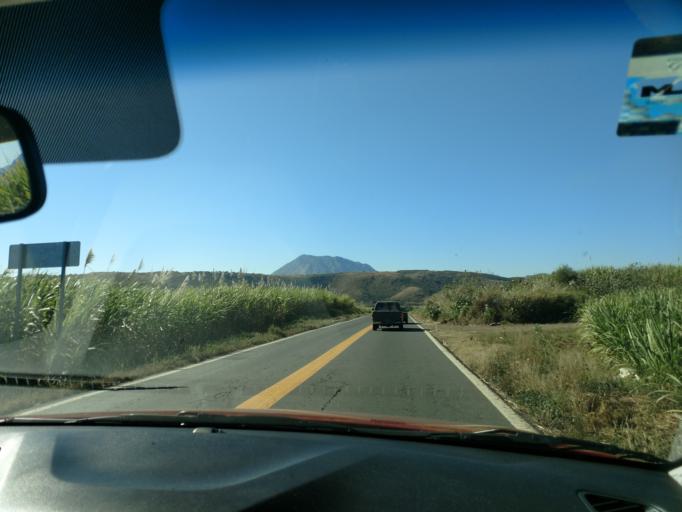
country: MX
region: Nayarit
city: San Pedro Lagunillas
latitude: 21.1506
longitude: -104.6124
